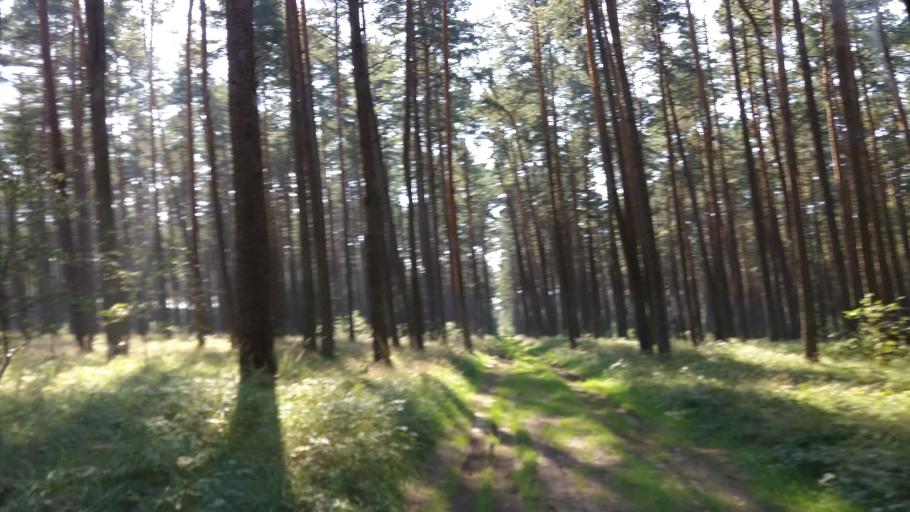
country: PL
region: West Pomeranian Voivodeship
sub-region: Powiat walecki
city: Tuczno
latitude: 53.2196
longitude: 16.0201
